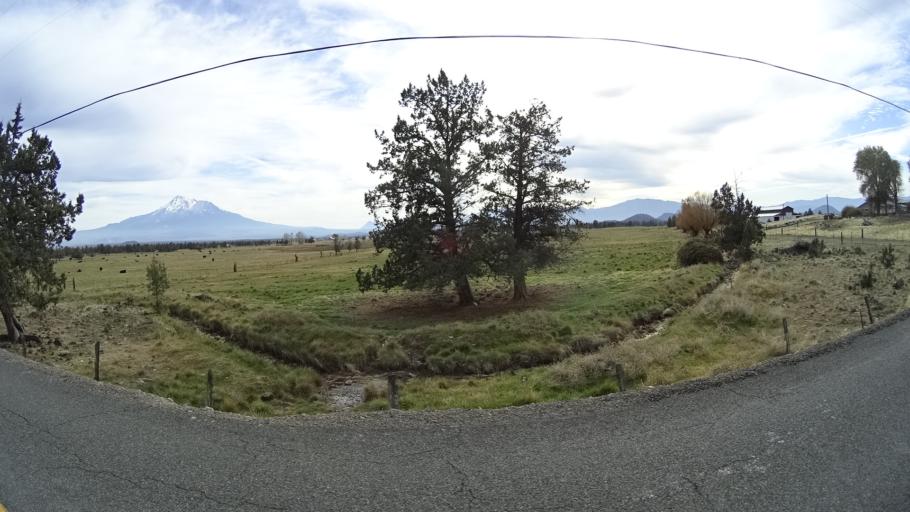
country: US
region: California
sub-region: Siskiyou County
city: Montague
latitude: 41.6384
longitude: -122.4146
